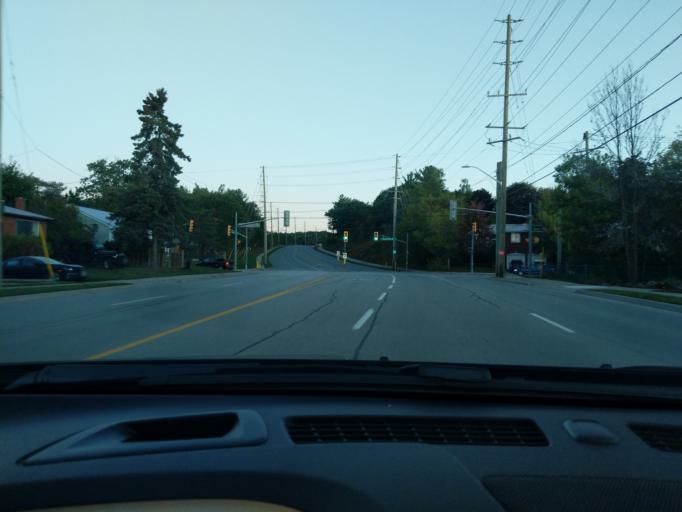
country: CA
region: Ontario
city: Barrie
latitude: 44.3808
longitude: -79.7240
